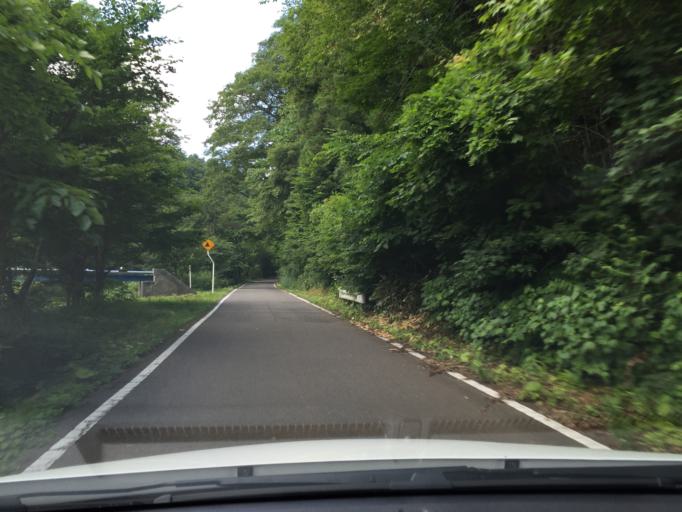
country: JP
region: Fukushima
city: Inawashiro
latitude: 37.2851
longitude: 140.0639
